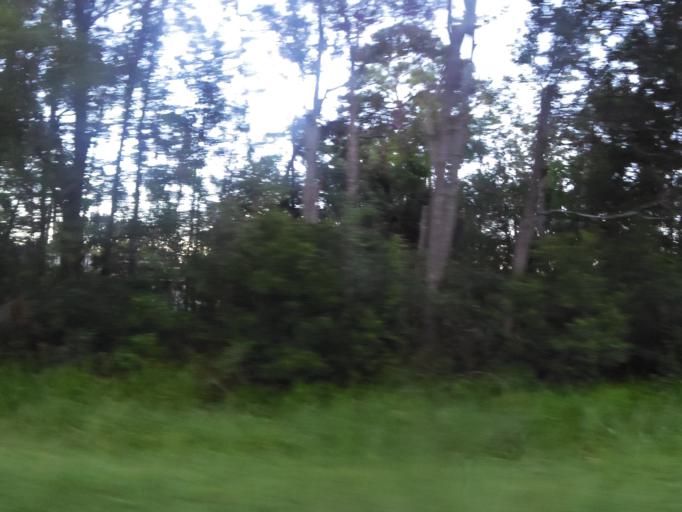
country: US
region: Georgia
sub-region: Camden County
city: St. Marys
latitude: 30.7370
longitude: -81.5480
